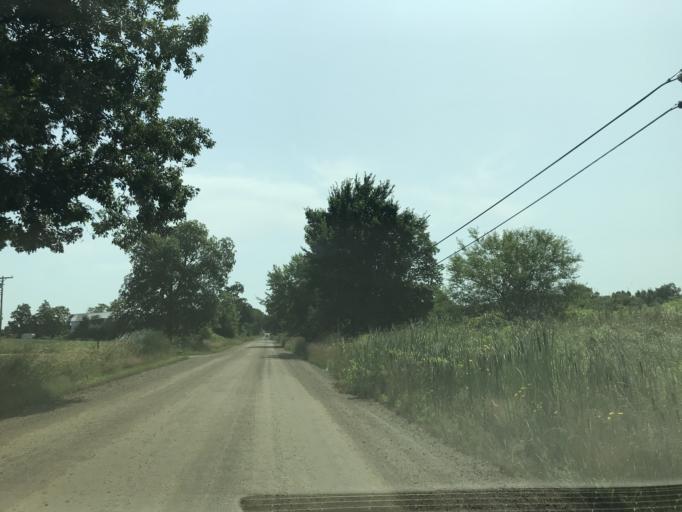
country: US
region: Michigan
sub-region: Eaton County
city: Grand Ledge
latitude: 42.7702
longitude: -84.7164
